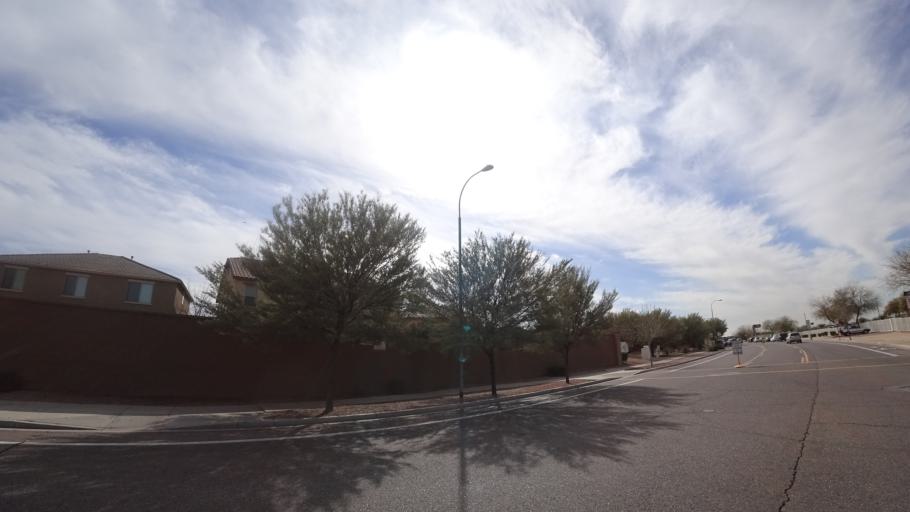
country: US
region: Arizona
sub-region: Maricopa County
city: Tolleson
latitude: 33.4730
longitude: -112.2613
